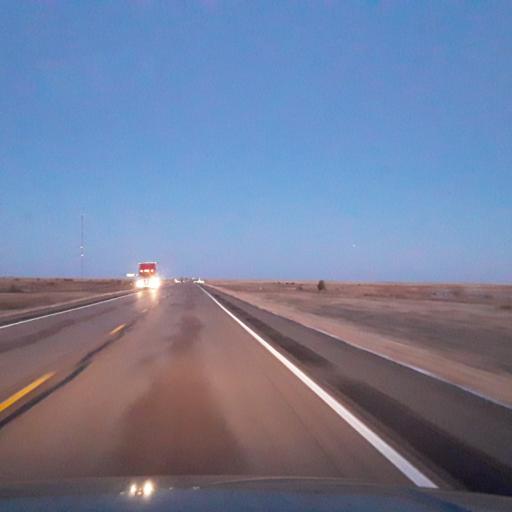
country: US
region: New Mexico
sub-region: Guadalupe County
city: Santa Rosa
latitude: 34.7810
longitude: -104.9422
